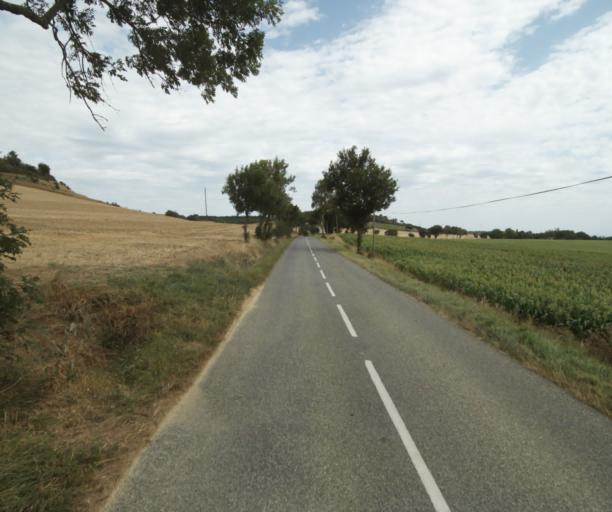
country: FR
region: Midi-Pyrenees
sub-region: Departement de la Haute-Garonne
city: Saint-Felix-Lauragais
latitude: 43.4372
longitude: 1.8978
